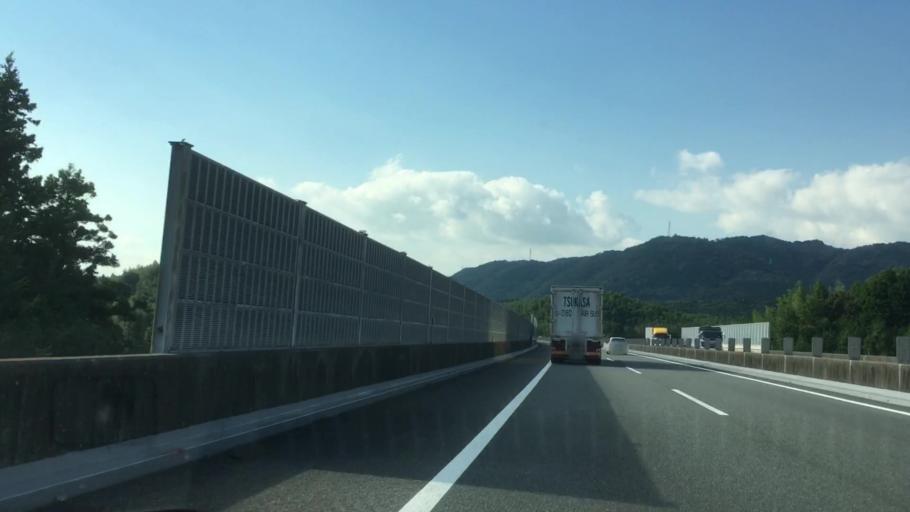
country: JP
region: Yamaguchi
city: Kudamatsu
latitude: 34.0375
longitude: 131.9251
